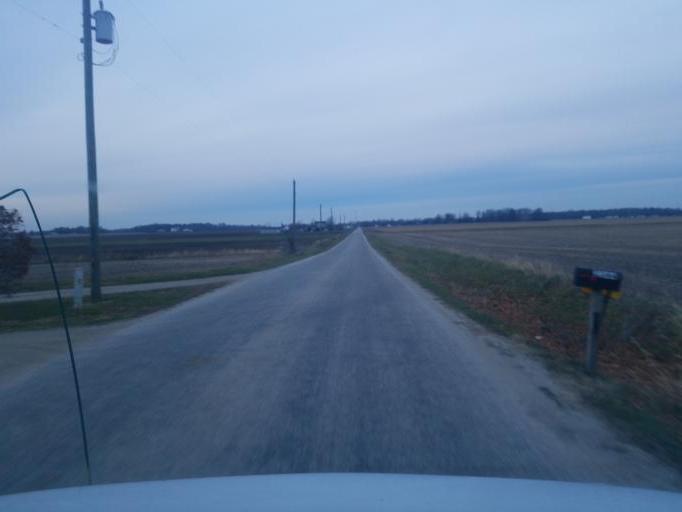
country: US
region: Indiana
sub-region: Adams County
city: Decatur
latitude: 40.7801
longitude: -84.8799
